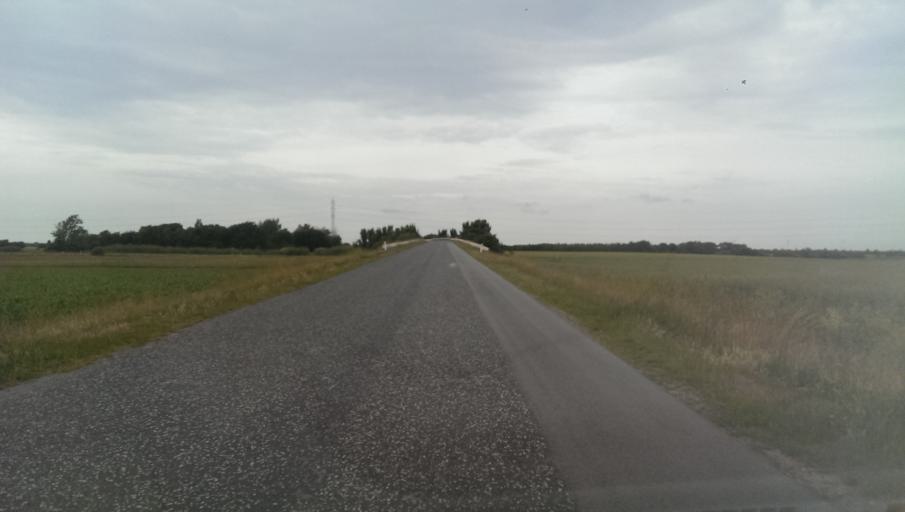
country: DK
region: South Denmark
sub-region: Esbjerg Kommune
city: Bramming
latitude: 55.4351
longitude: 8.6499
